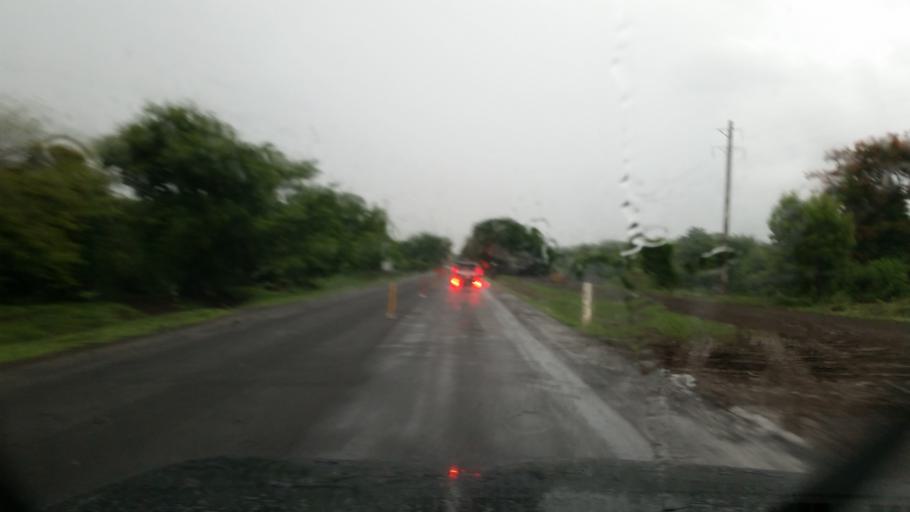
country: NI
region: Chinandega
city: Chichigalpa
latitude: 12.7880
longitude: -86.9483
